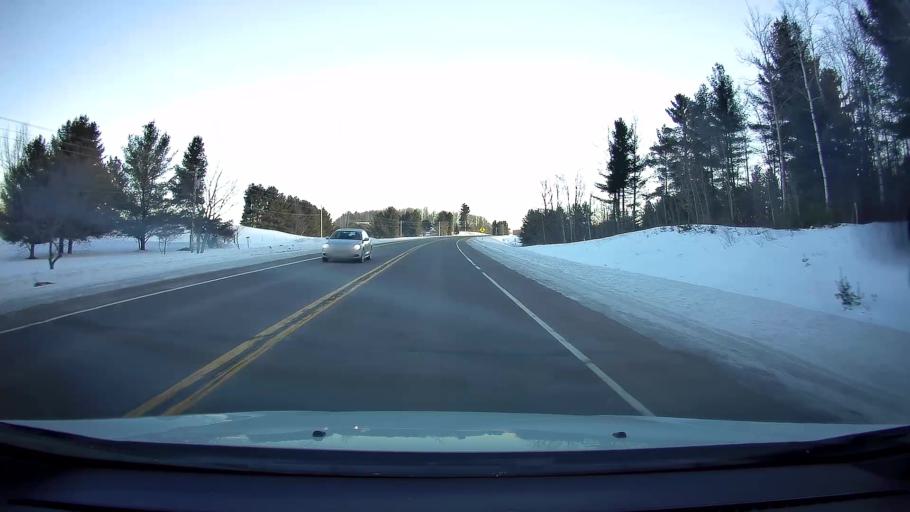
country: US
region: Wisconsin
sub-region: Barron County
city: Cumberland
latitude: 45.6001
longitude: -92.0172
